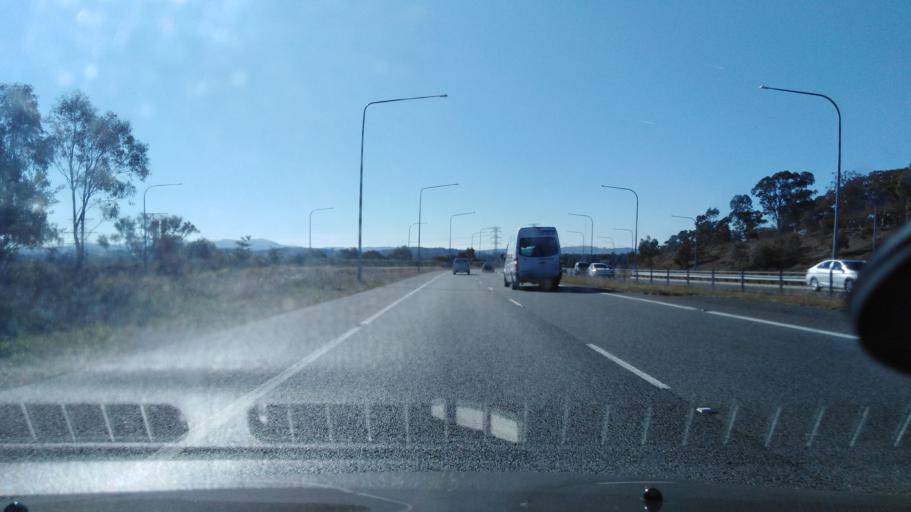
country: AU
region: Australian Capital Territory
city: Kaleen
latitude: -35.2425
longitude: 149.1107
